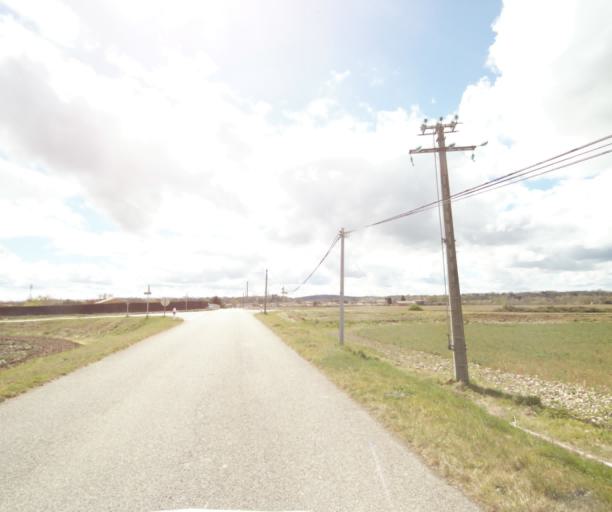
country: FR
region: Midi-Pyrenees
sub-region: Departement de l'Ariege
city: Saverdun
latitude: 43.2412
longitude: 1.5859
